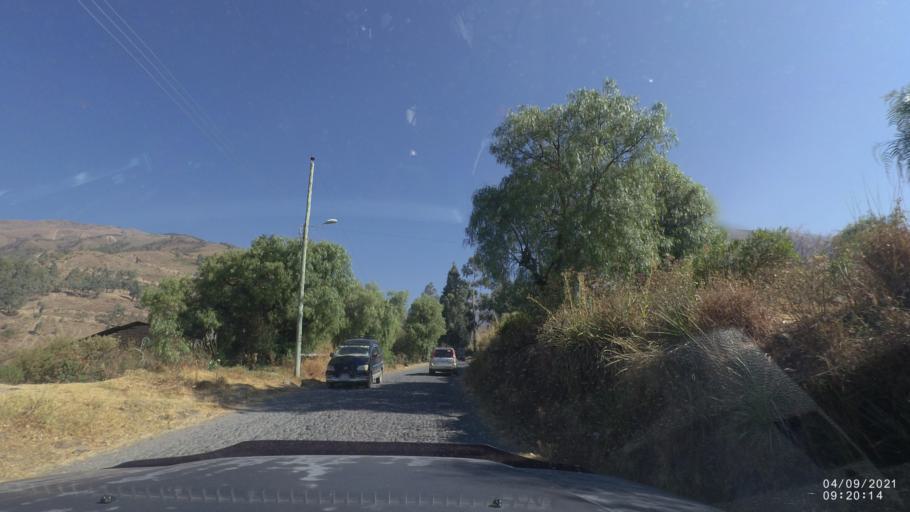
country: BO
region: Cochabamba
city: Sipe Sipe
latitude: -17.3645
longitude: -66.3618
